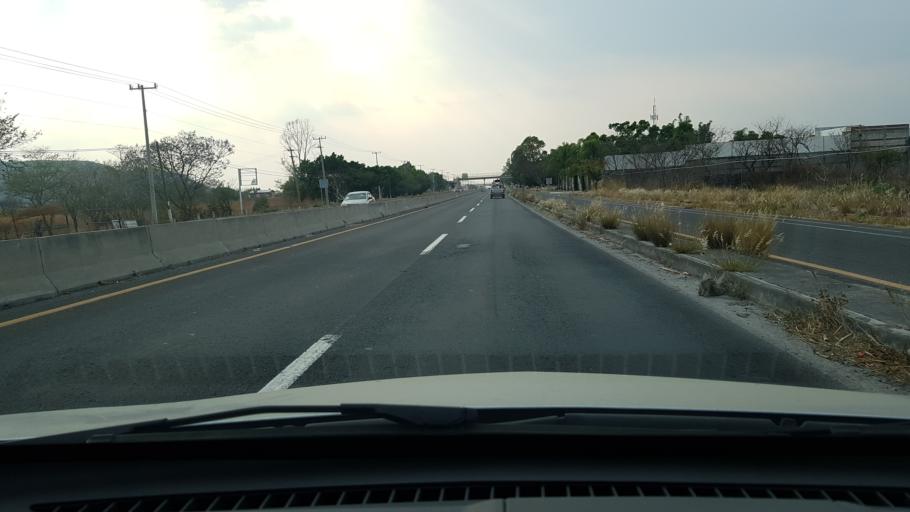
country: MX
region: Morelos
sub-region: Ayala
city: Unidad Habitacional Mariano Matamoros
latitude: 18.7470
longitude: -98.8438
